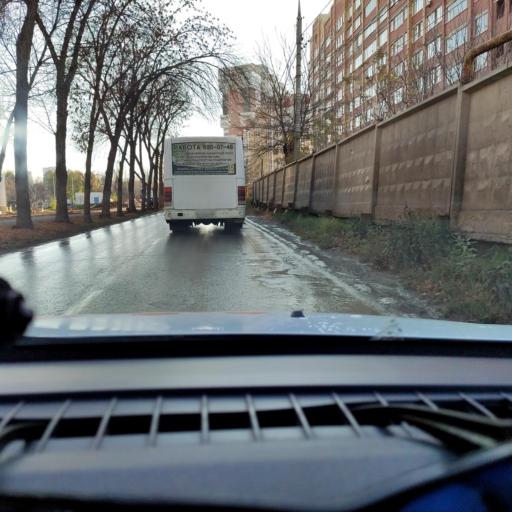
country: RU
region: Samara
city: Samara
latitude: 53.2401
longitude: 50.1784
